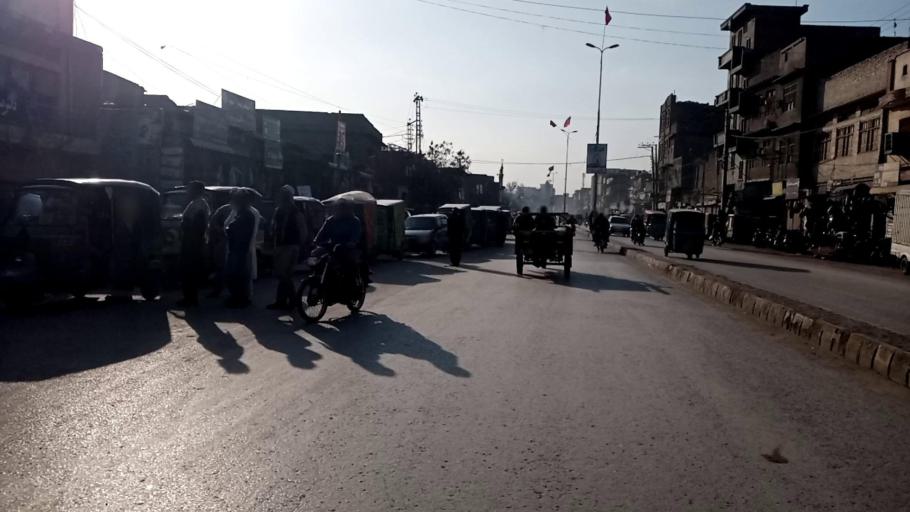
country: PK
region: Khyber Pakhtunkhwa
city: Peshawar
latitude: 34.0047
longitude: 71.5752
